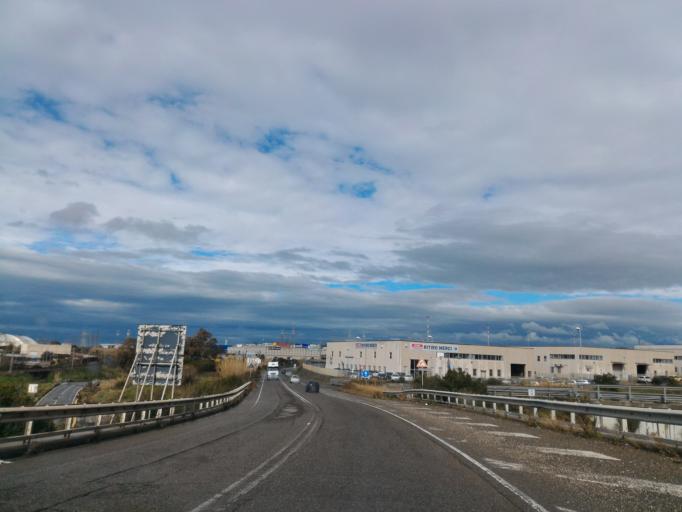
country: IT
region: Latium
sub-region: Citta metropolitana di Roma Capitale
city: Aurelia
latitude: 42.1205
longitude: 11.7710
